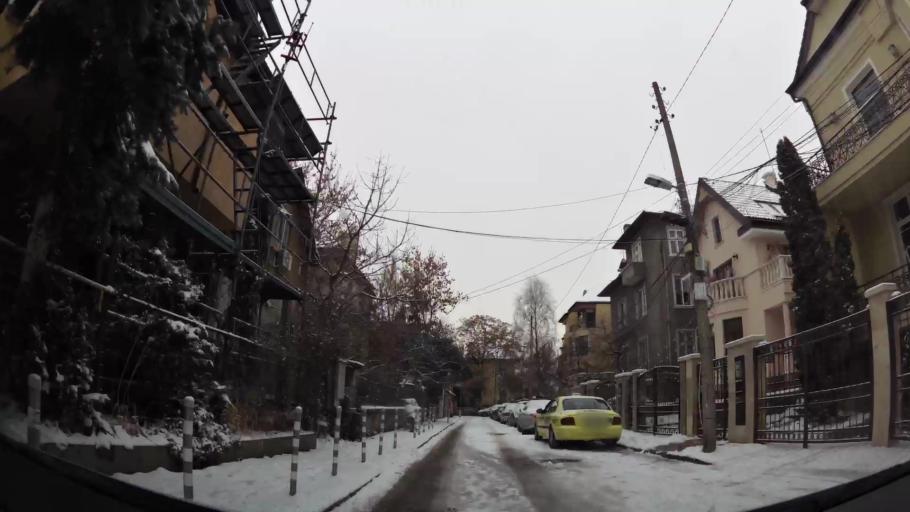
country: BG
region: Sofia-Capital
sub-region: Stolichna Obshtina
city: Sofia
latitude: 42.6895
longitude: 23.3457
